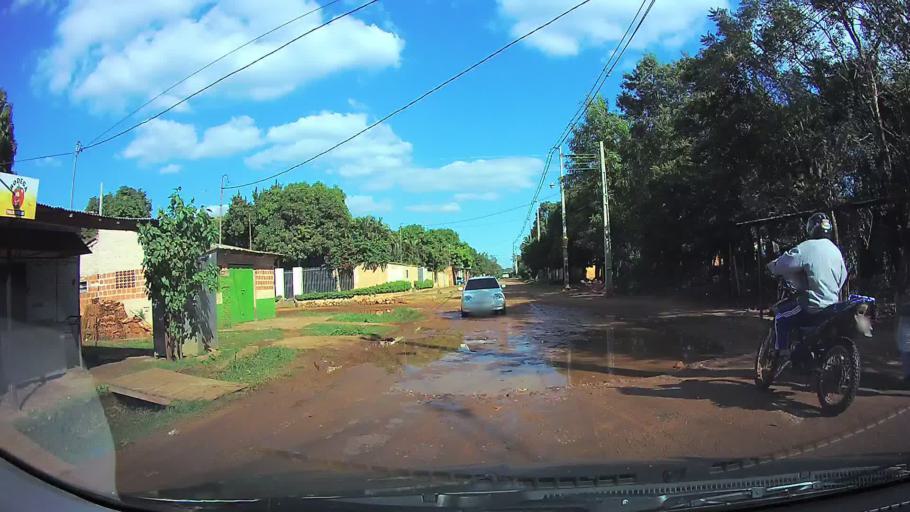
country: PY
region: Central
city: Limpio
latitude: -25.2408
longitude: -57.4745
